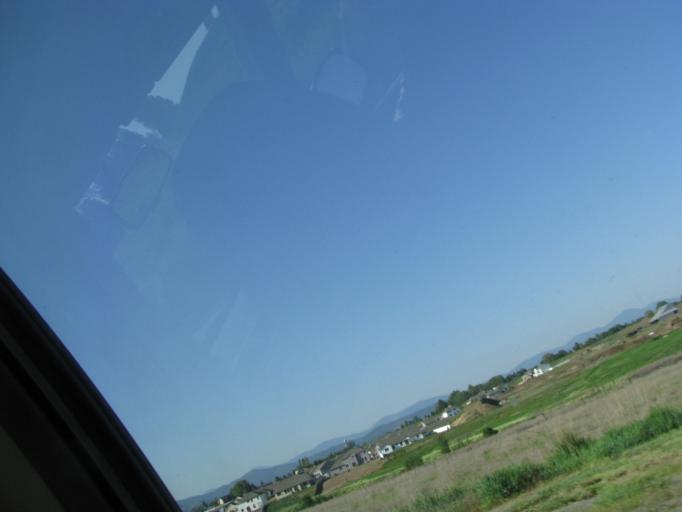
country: US
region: Washington
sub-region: Spokane County
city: Liberty Lake
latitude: 47.6396
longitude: -117.1487
